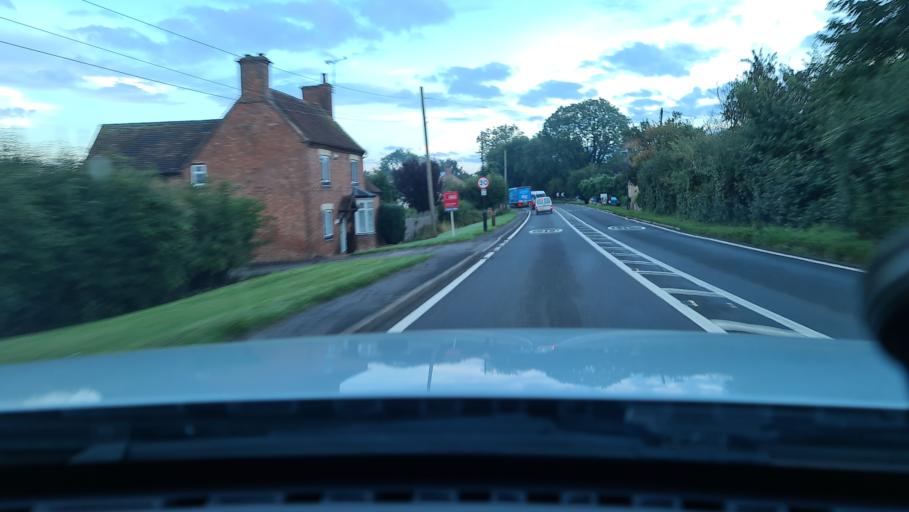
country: GB
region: England
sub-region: Warwickshire
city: Long Itchington
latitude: 52.2894
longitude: -1.3937
